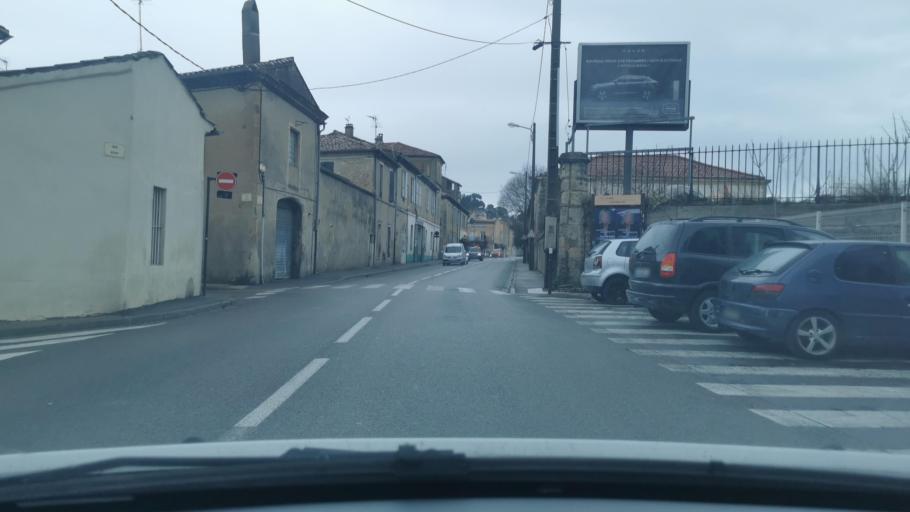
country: FR
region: Languedoc-Roussillon
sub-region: Departement du Gard
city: Nimes
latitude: 43.8422
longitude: 4.3706
